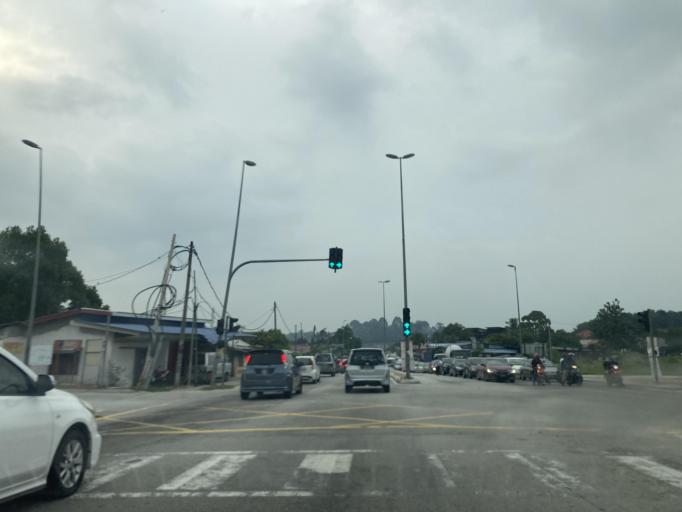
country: MY
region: Selangor
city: Kuang
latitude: 3.2077
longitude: 101.5396
